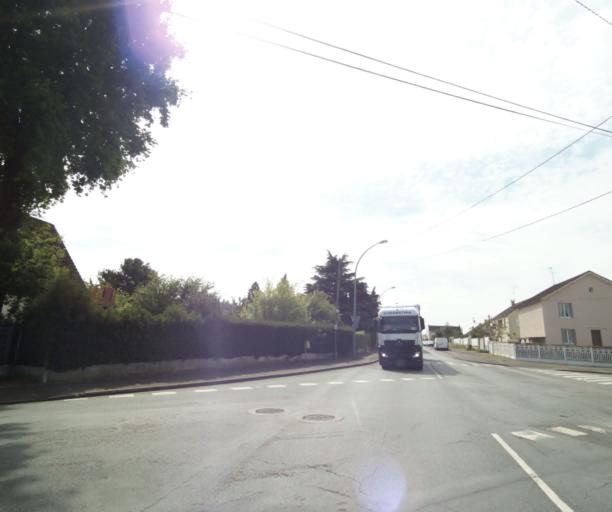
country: FR
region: Ile-de-France
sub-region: Departement des Yvelines
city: Les Mureaux
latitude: 48.9907
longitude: 1.8974
